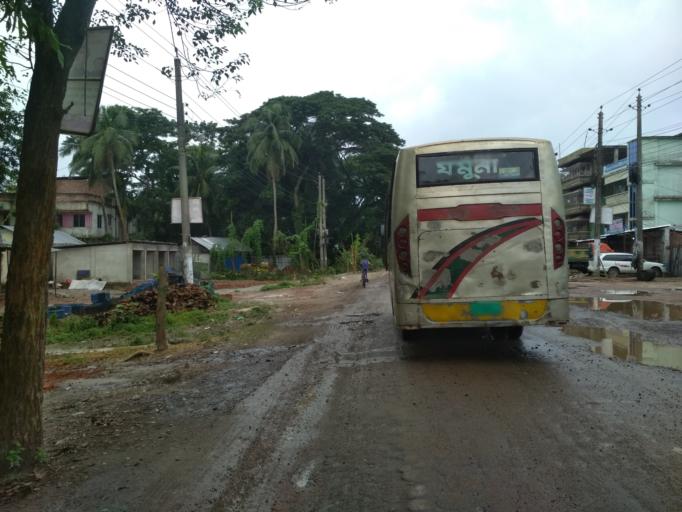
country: BD
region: Chittagong
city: Lakshmipur
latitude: 22.9458
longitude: 90.8178
